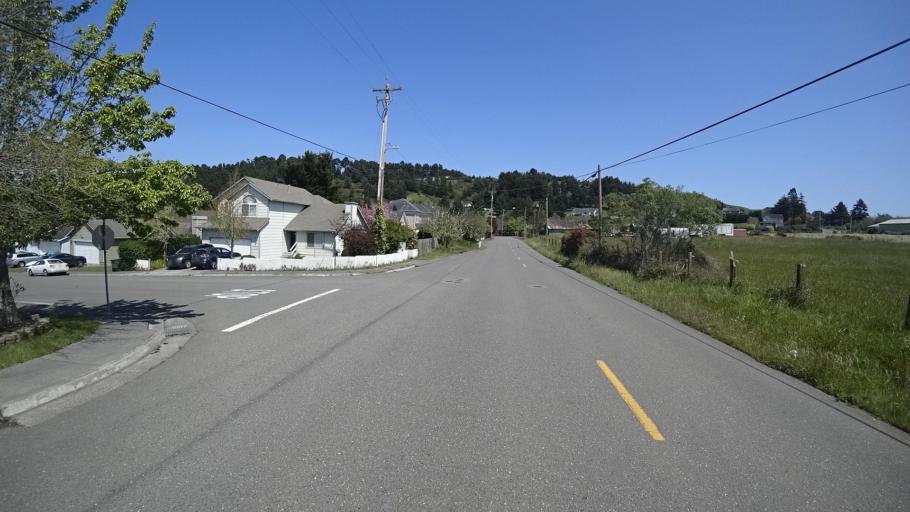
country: US
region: California
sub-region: Humboldt County
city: Hydesville
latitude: 40.5630
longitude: -124.1287
